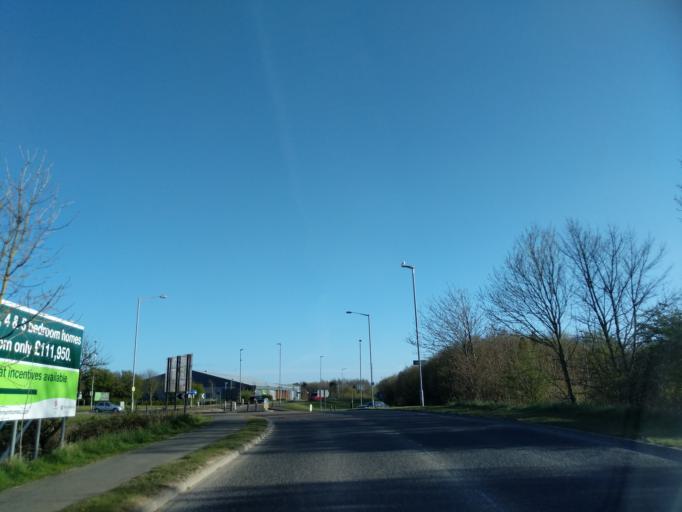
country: GB
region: England
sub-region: Northumberland
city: Cramlington
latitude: 55.0881
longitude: -1.5964
